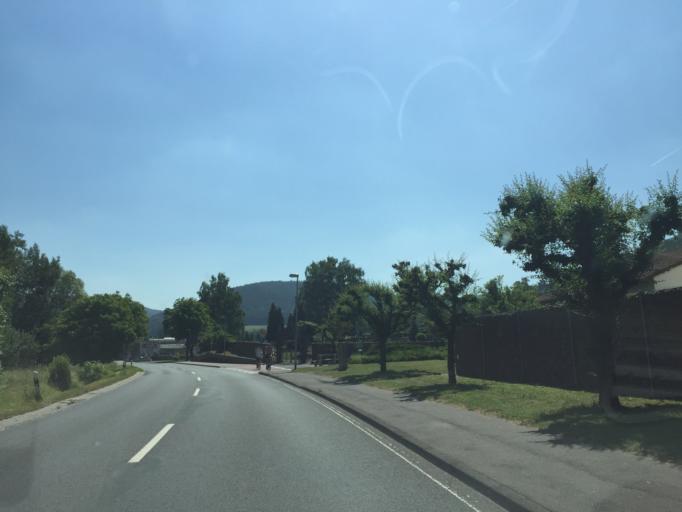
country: DE
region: Bavaria
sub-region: Regierungsbezirk Unterfranken
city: Weilbach
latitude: 49.6425
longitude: 9.2299
